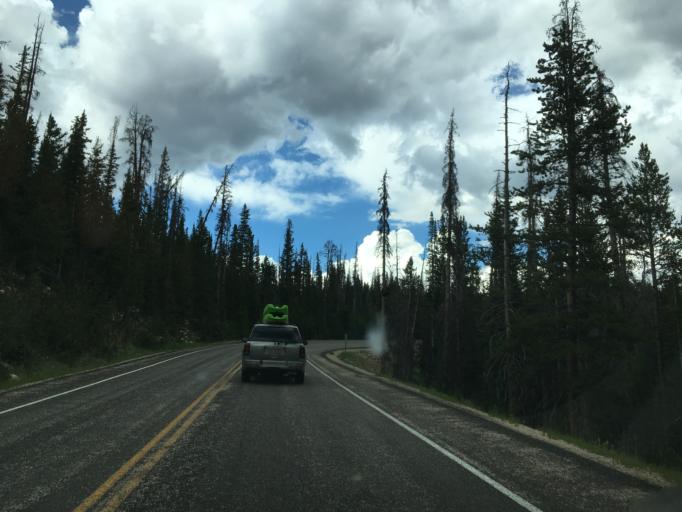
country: US
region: Utah
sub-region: Summit County
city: Kamas
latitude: 40.6755
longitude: -110.9464
